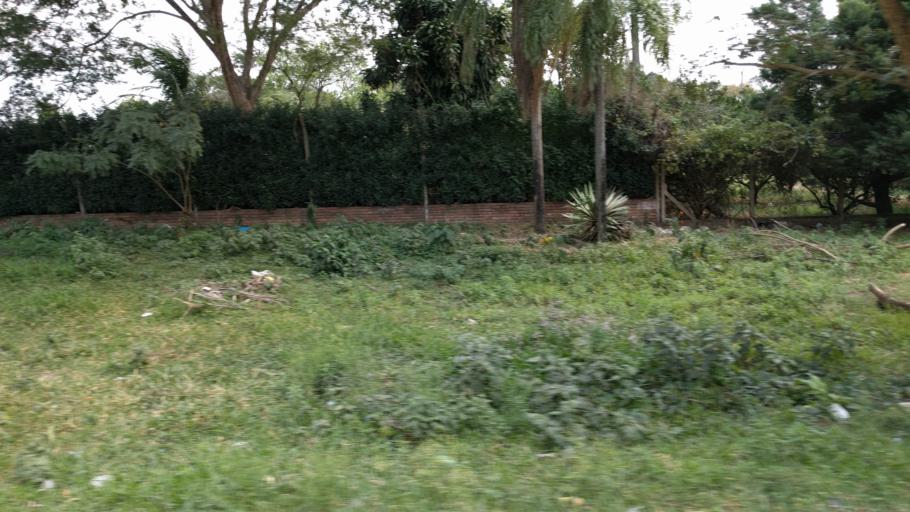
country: BO
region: Santa Cruz
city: Santa Rita
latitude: -17.9039
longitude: -63.3397
